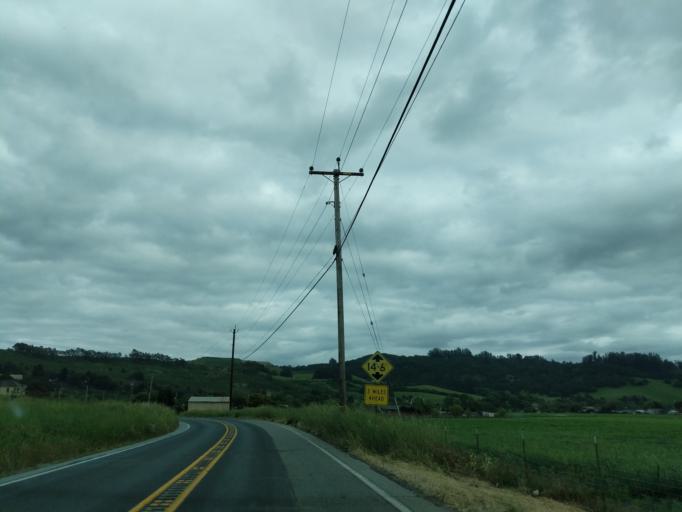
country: US
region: California
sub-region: San Benito County
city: Aromas
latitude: 36.9043
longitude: -121.6441
